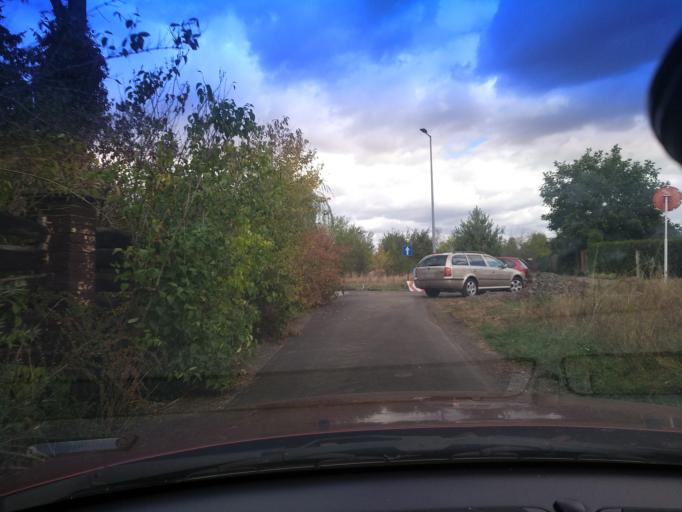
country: PL
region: Lower Silesian Voivodeship
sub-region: Powiat zgorzelecki
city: Zgorzelec
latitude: 51.1898
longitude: 15.0097
